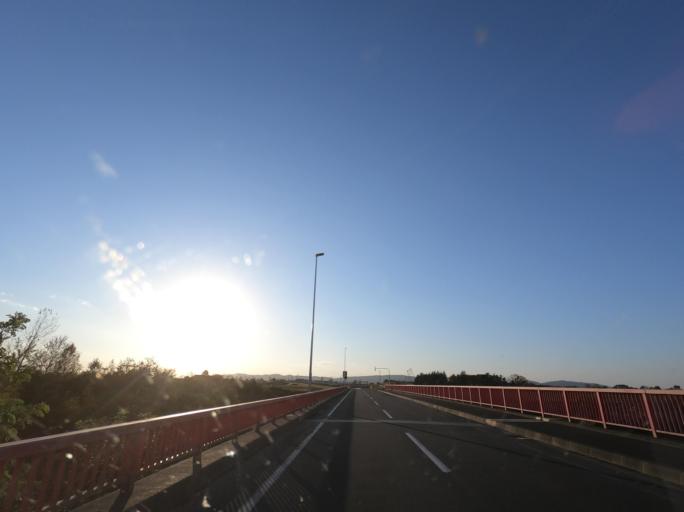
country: JP
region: Hokkaido
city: Iwamizawa
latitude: 42.9784
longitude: 141.8601
